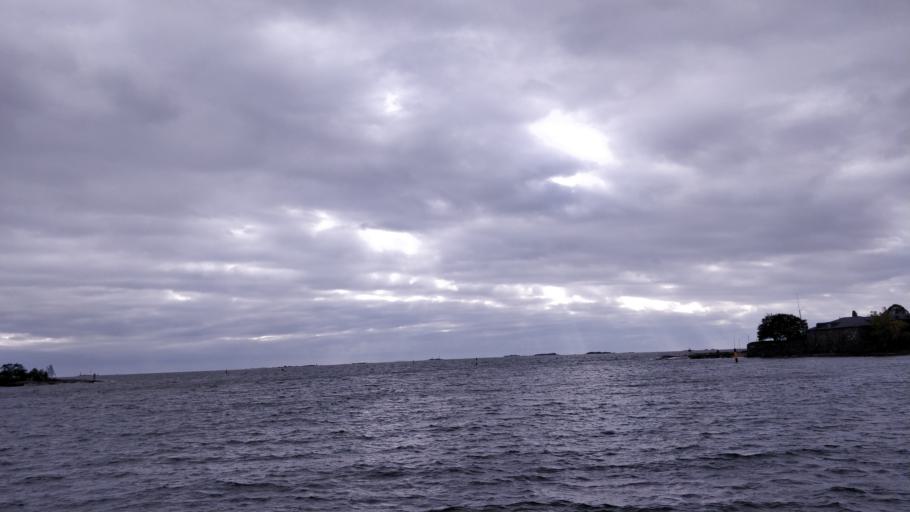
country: FI
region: Uusimaa
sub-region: Helsinki
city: Helsinki
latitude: 60.1519
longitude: 24.9709
